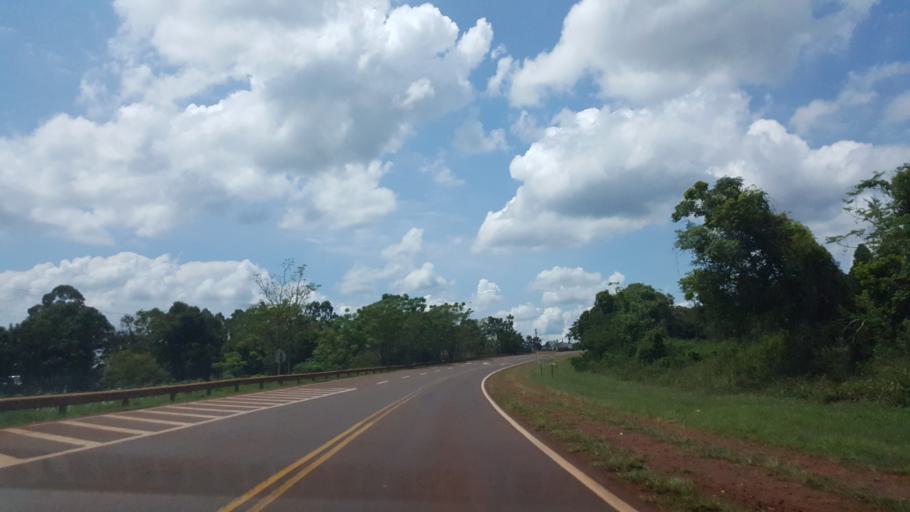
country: AR
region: Misiones
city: Garuhape
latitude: -26.8118
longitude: -54.9394
